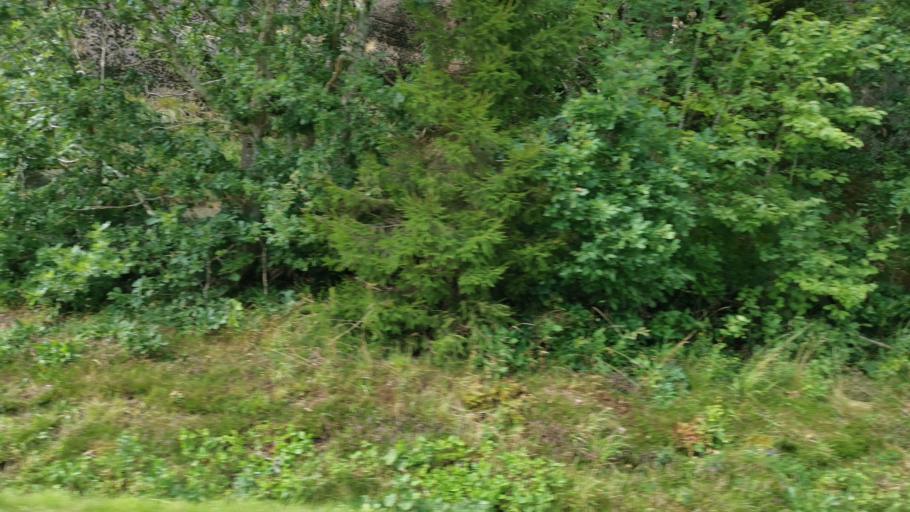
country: SE
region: Vaestra Goetaland
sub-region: Lysekils Kommun
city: Brastad
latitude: 58.4637
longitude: 11.4577
